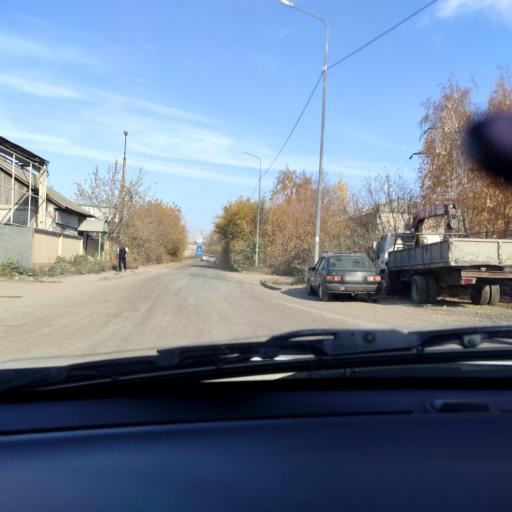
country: RU
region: Tatarstan
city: Verkhniy Uslon
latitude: 55.8023
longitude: 49.0465
